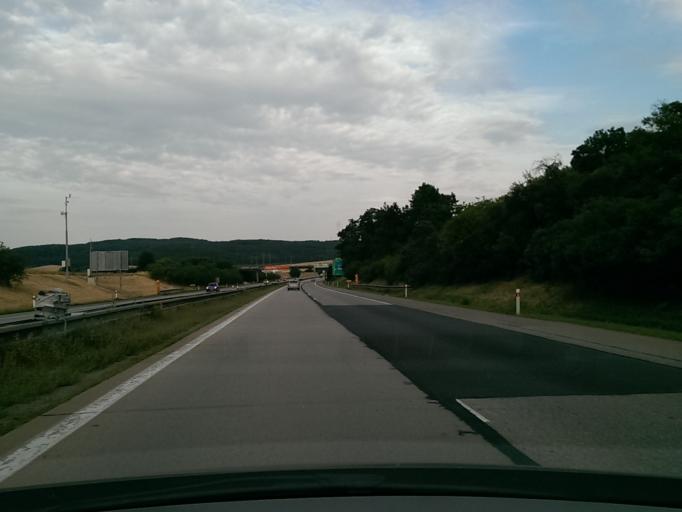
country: CZ
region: South Moravian
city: Ricany
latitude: 49.2207
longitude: 16.3996
